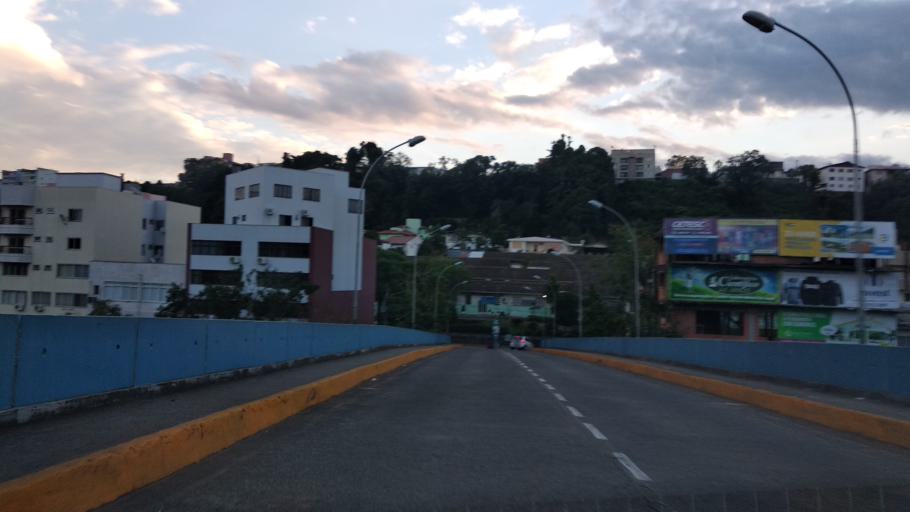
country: BR
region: Santa Catarina
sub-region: Videira
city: Videira
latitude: -27.0014
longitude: -51.1572
